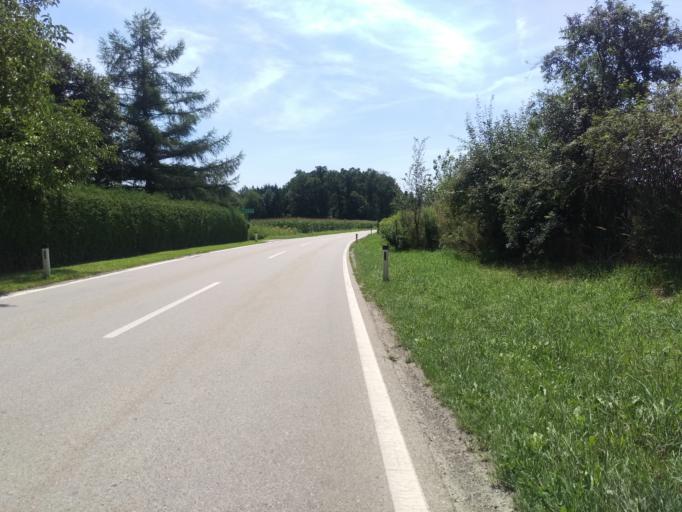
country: AT
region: Styria
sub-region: Politischer Bezirk Graz-Umgebung
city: Zettling
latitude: 46.9735
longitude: 15.4391
